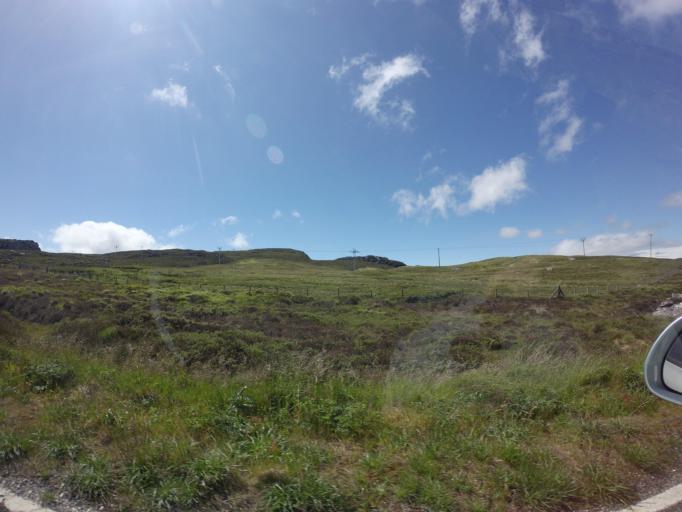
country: GB
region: Scotland
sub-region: Eilean Siar
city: Stornoway
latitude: 58.1427
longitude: -6.5081
